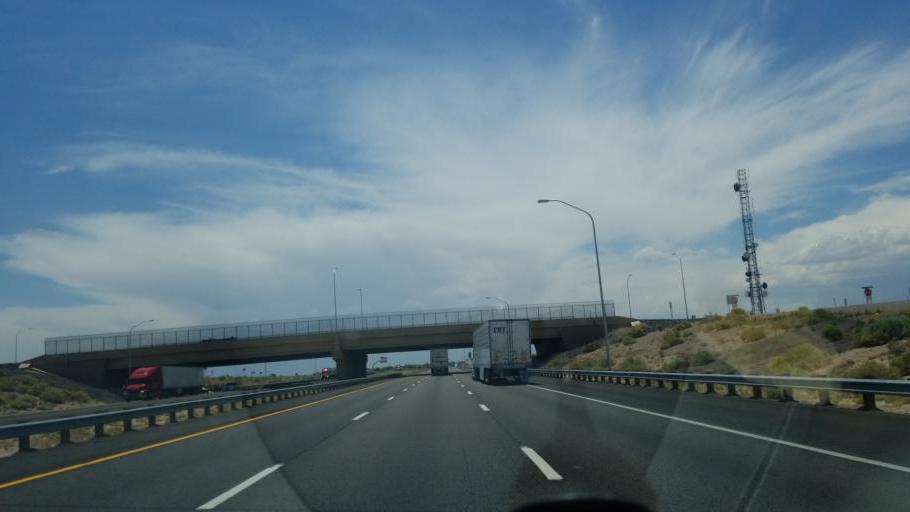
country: US
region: New Mexico
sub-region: Bernalillo County
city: South Valley
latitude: 35.0659
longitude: -106.7865
